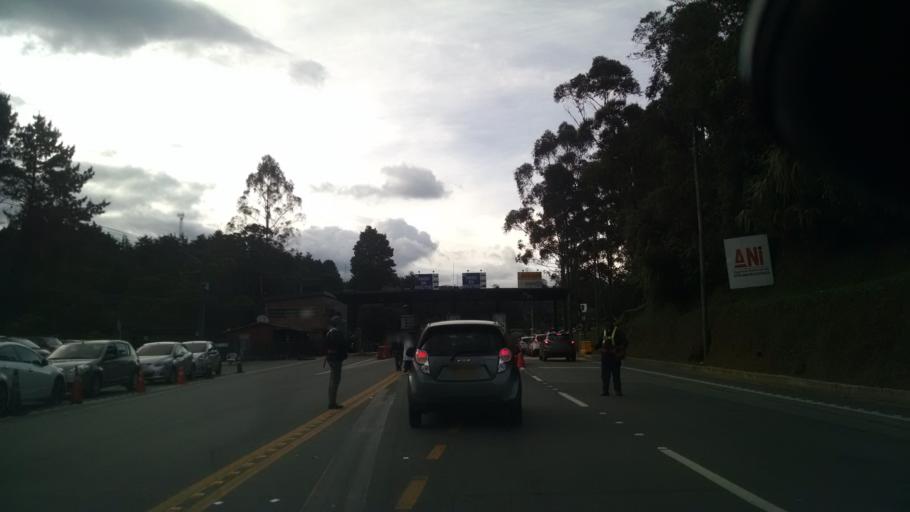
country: CO
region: Antioquia
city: Envigado
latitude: 6.1502
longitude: -75.5307
